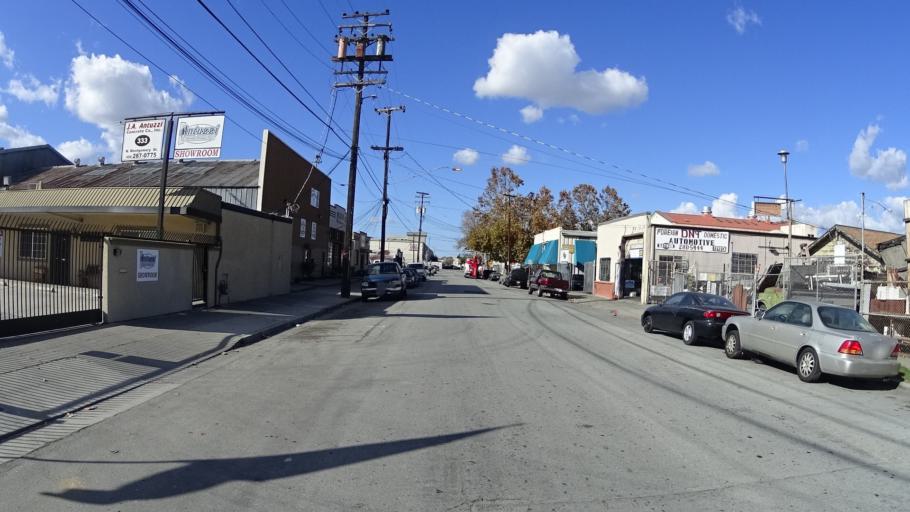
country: US
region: California
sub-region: Santa Clara County
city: San Jose
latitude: 37.3359
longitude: -121.9040
